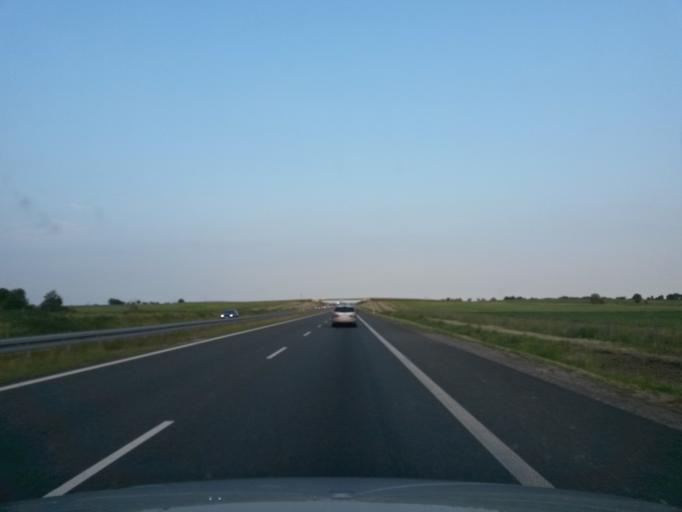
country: PL
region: Lower Silesian Voivodeship
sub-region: Powiat olesnicki
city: Sycow
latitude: 51.3007
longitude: 17.6452
